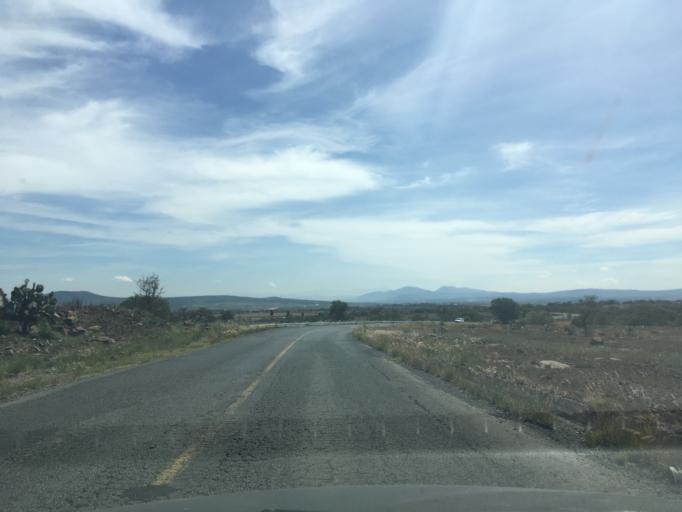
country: MX
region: Queretaro
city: Amealco
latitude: 20.2387
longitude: -100.0846
